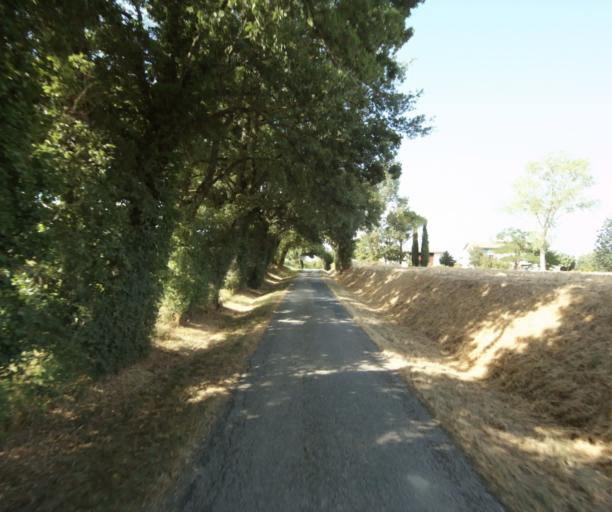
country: FR
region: Midi-Pyrenees
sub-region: Departement du Tarn
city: Puylaurens
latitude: 43.5250
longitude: 1.9894
